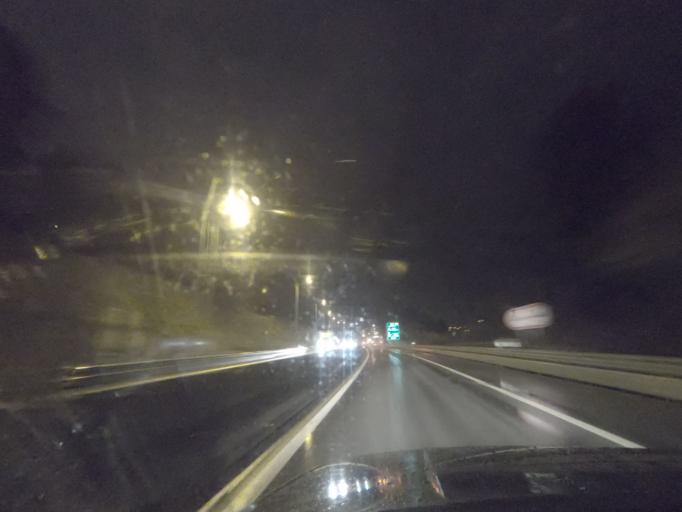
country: PT
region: Vila Real
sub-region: Vila Real
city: Vila Real
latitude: 41.3070
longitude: -7.7509
